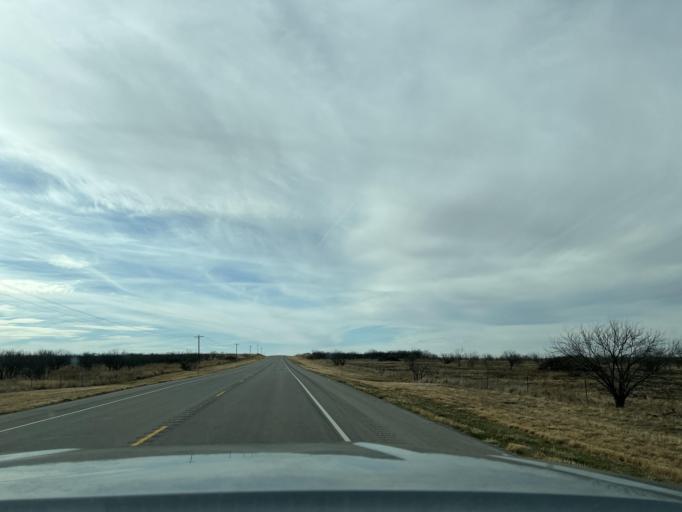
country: US
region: Texas
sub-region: Jones County
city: Anson
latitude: 32.7505
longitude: -99.6742
